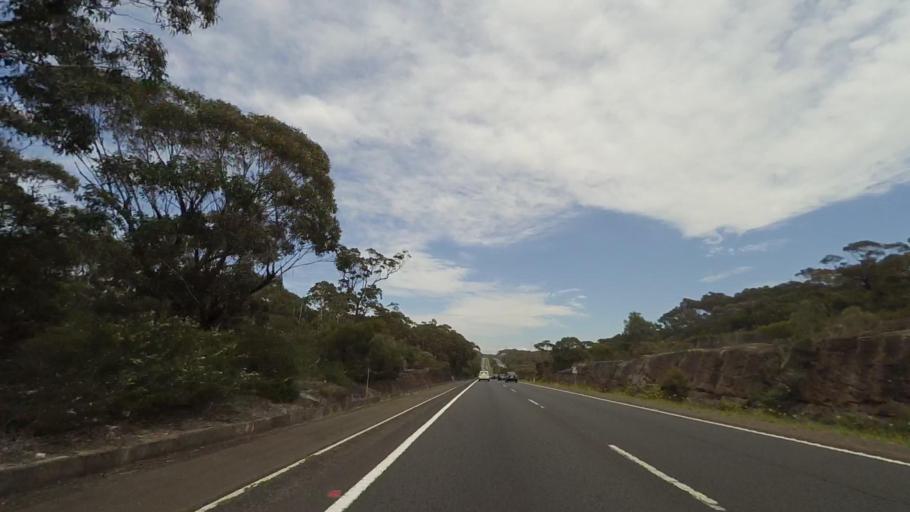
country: AU
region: New South Wales
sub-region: Wollongong
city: Helensburgh
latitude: -34.2131
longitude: 150.9591
